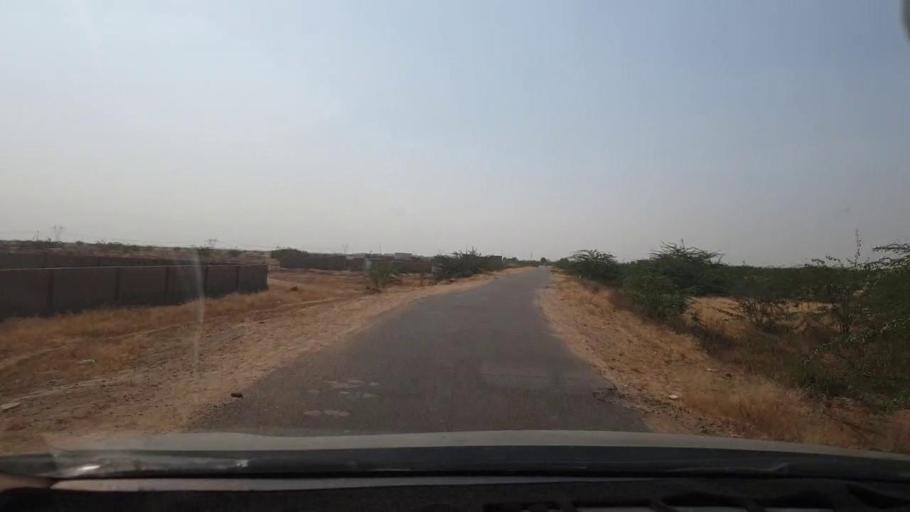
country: PK
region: Sindh
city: Malir Cantonment
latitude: 25.1245
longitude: 67.2222
